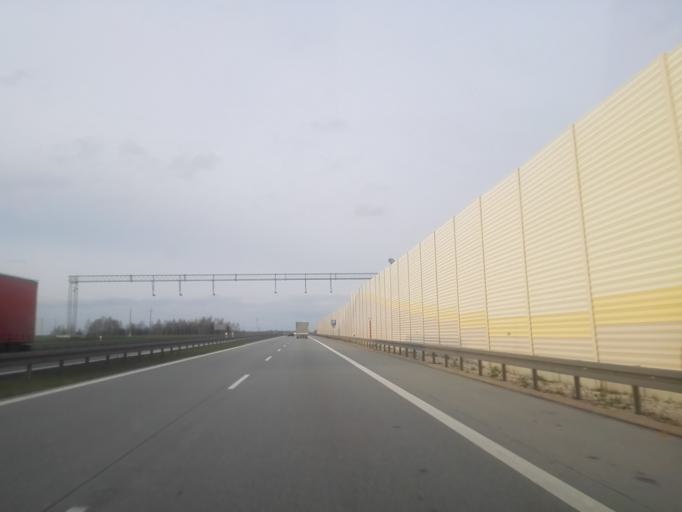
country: PL
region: Lodz Voivodeship
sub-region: Powiat skierniewicki
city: Kowiesy
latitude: 51.8554
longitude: 20.3744
